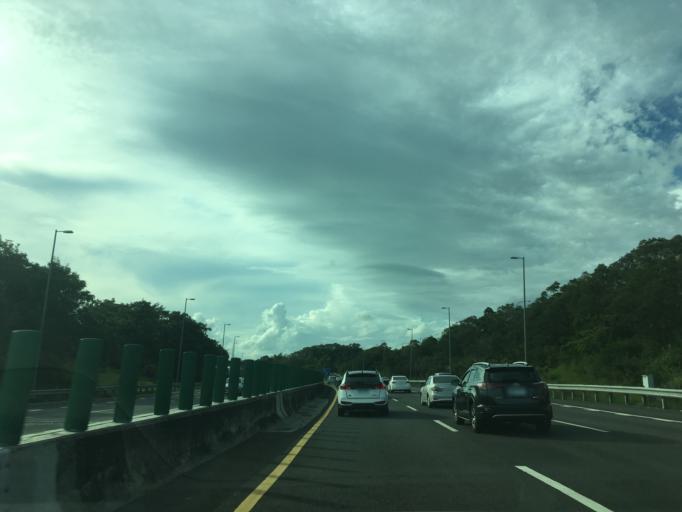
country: TW
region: Taiwan
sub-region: Nantou
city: Nantou
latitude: 23.8969
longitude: 120.7103
